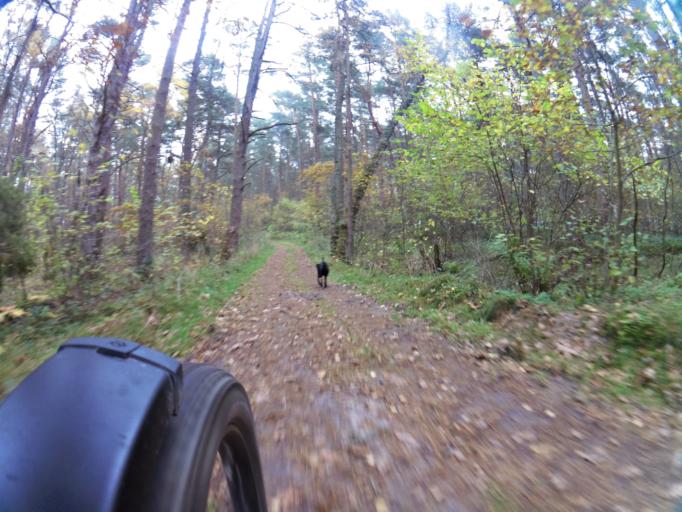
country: PL
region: Pomeranian Voivodeship
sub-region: Powiat pucki
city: Krokowa
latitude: 54.8297
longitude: 18.1222
